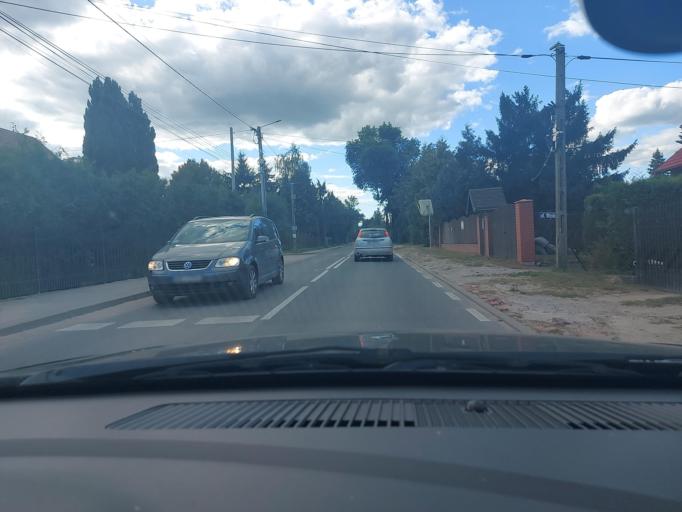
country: PL
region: Masovian Voivodeship
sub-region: Powiat nowodworski
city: Pomiechowek
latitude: 52.4909
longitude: 20.7065
